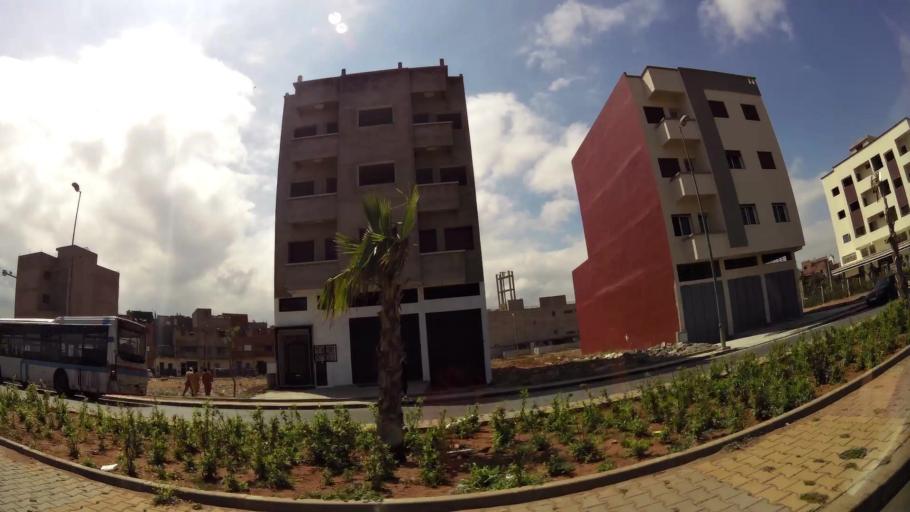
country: MA
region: Rabat-Sale-Zemmour-Zaer
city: Sale
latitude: 34.0716
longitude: -6.7716
